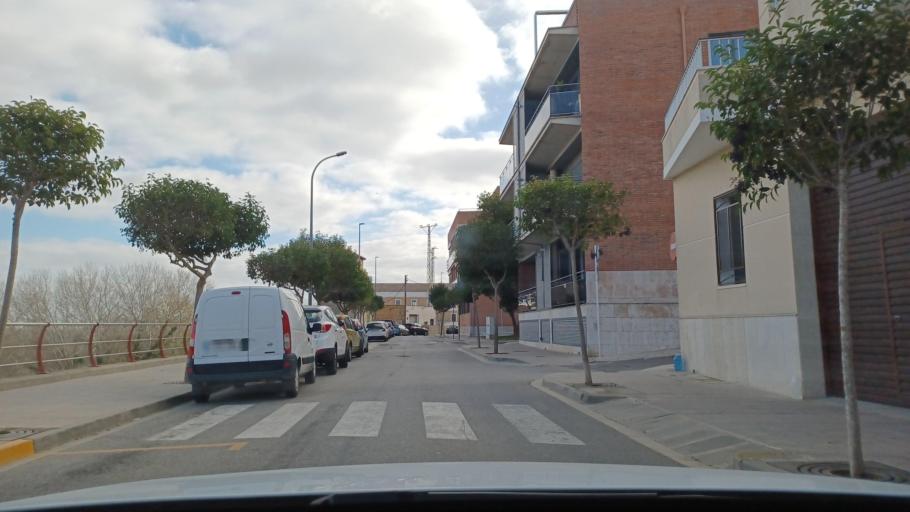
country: ES
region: Catalonia
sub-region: Provincia de Tarragona
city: Amposta
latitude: 40.7153
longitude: 0.5774
